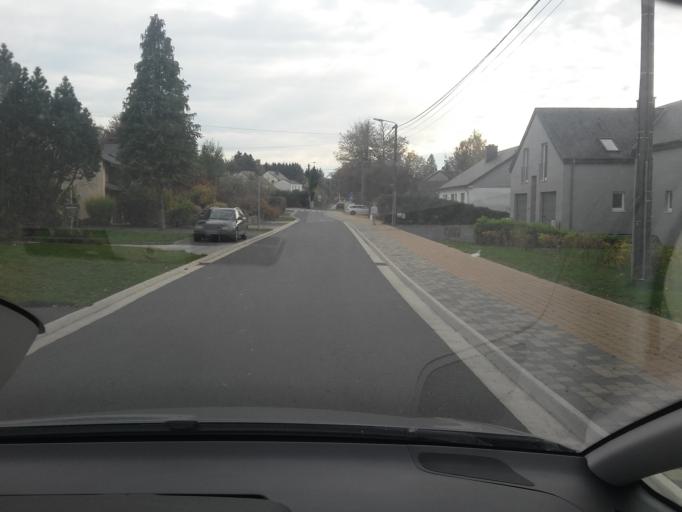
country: BE
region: Wallonia
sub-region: Province du Luxembourg
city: Arlon
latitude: 49.7023
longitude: 5.8194
